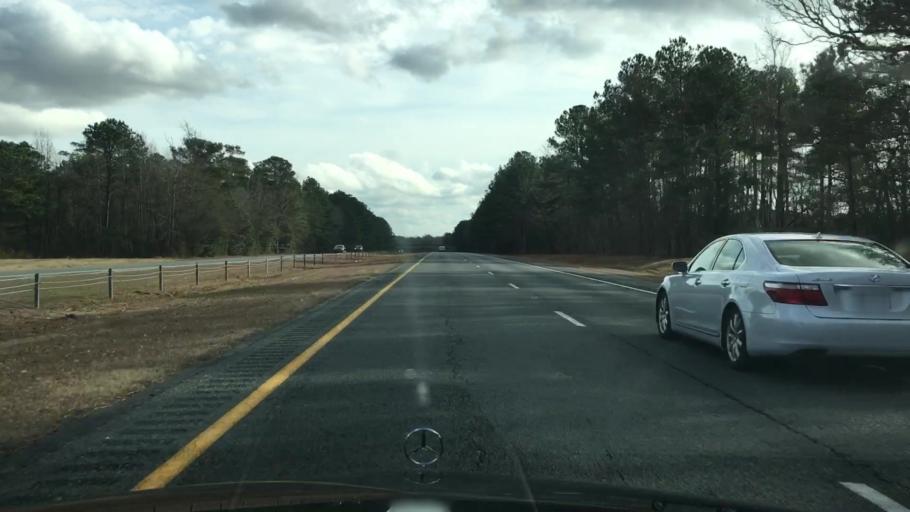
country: US
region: North Carolina
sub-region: Sampson County
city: Clinton
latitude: 35.2188
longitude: -78.3343
